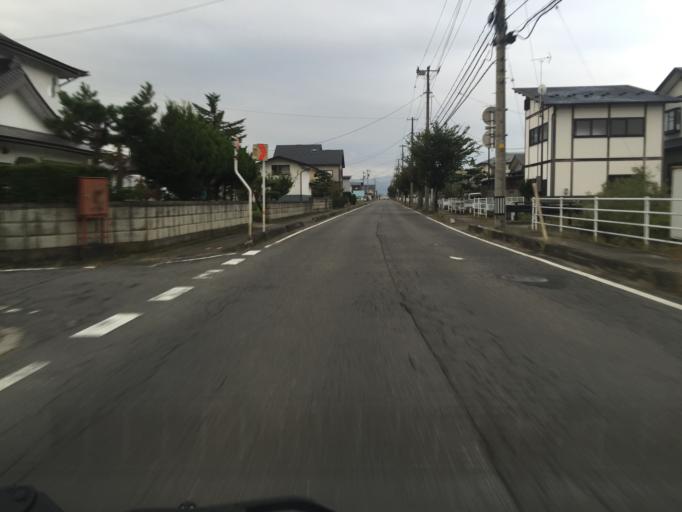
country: JP
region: Fukushima
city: Kitakata
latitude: 37.5162
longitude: 139.8769
